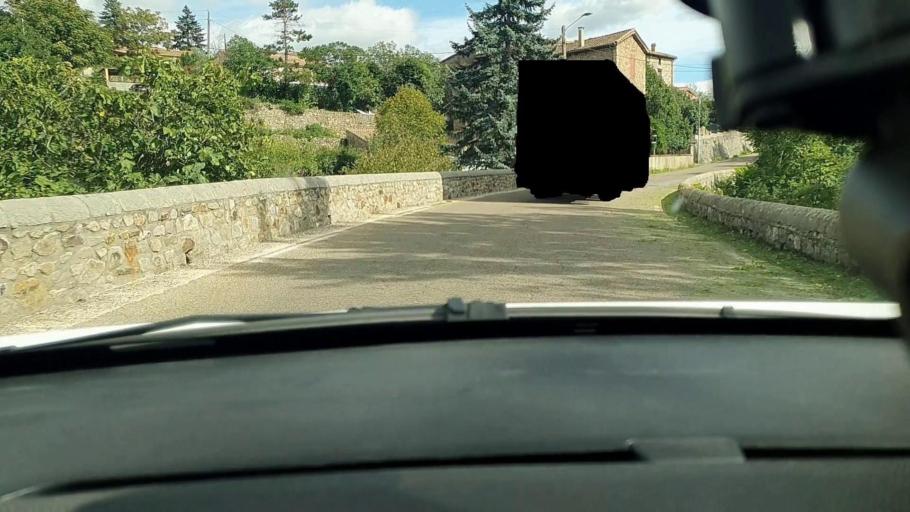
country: FR
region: Languedoc-Roussillon
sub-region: Departement du Gard
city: Saint-Florent-sur-Auzonnet
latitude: 44.2431
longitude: 4.1033
